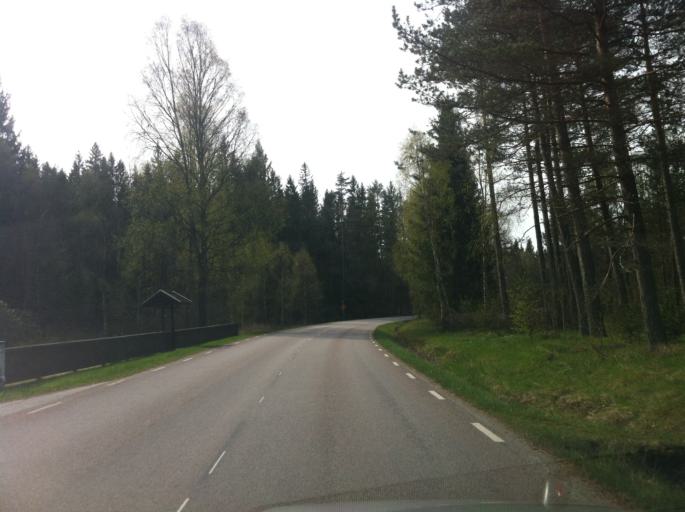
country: SE
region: Vaestra Goetaland
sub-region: Bollebygds Kommun
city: Bollebygd
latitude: 57.7096
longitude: 12.5818
